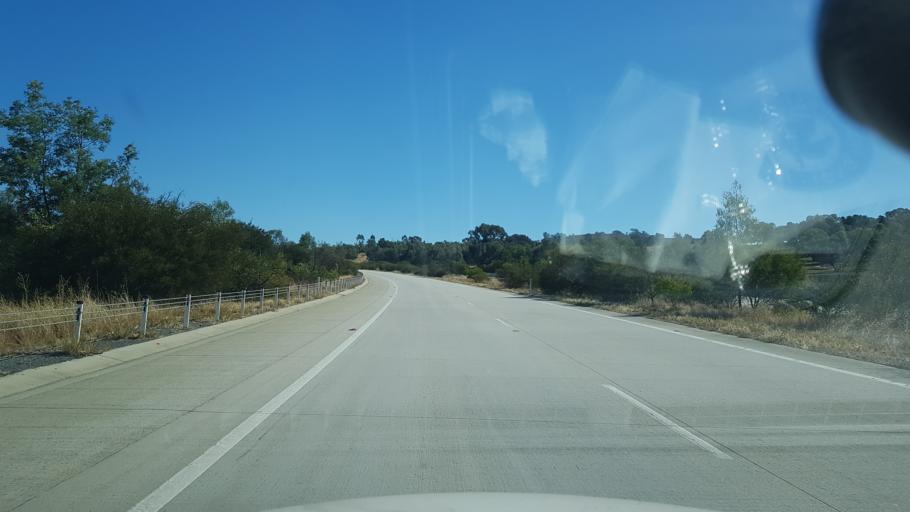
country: AU
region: New South Wales
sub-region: Albury Municipality
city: Lavington
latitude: -35.9158
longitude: 147.1027
